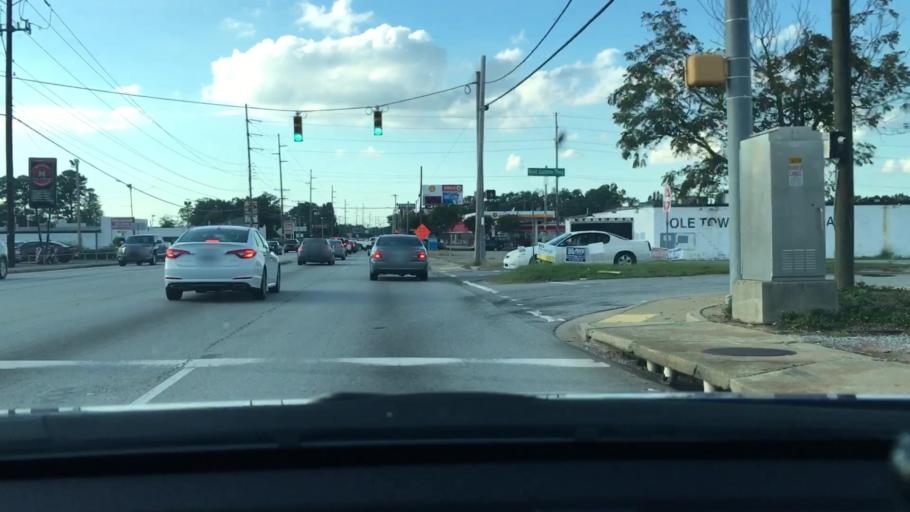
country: US
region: South Carolina
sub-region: Lexington County
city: Saint Andrews
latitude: 34.0478
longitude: -81.1032
